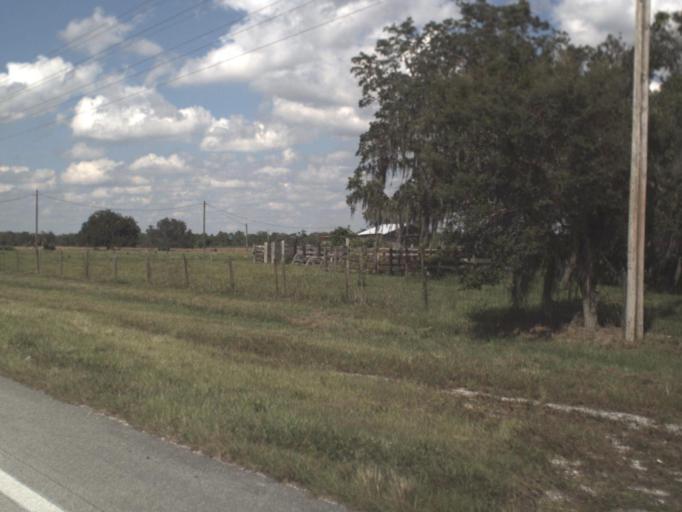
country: US
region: Florida
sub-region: Okeechobee County
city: Okeechobee
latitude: 27.3844
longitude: -80.9984
